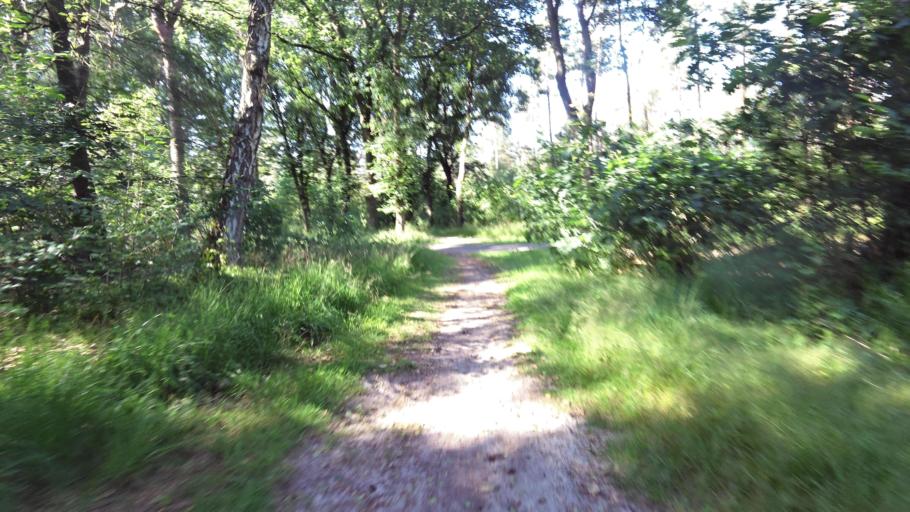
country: NL
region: Gelderland
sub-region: Gemeente Arnhem
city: Hoogkamp
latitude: 52.0145
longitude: 5.8871
